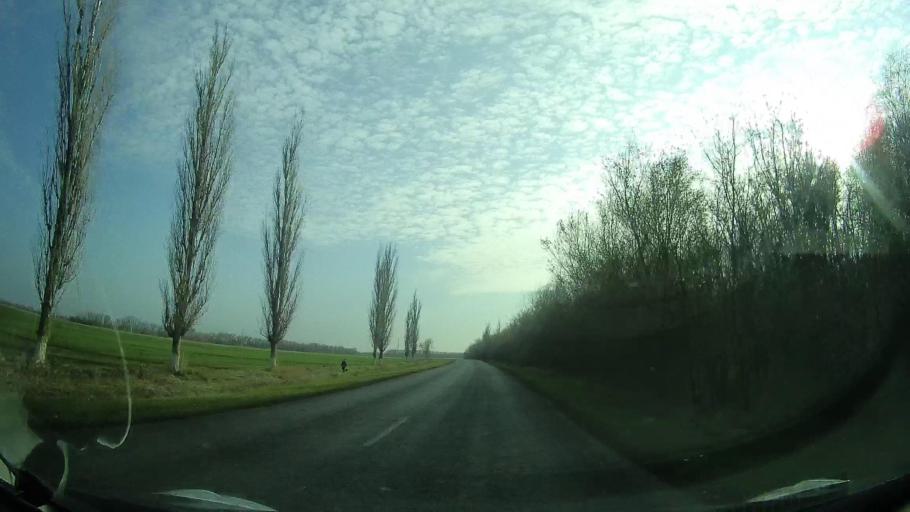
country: RU
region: Rostov
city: Mechetinskaya
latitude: 46.8217
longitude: 40.5548
